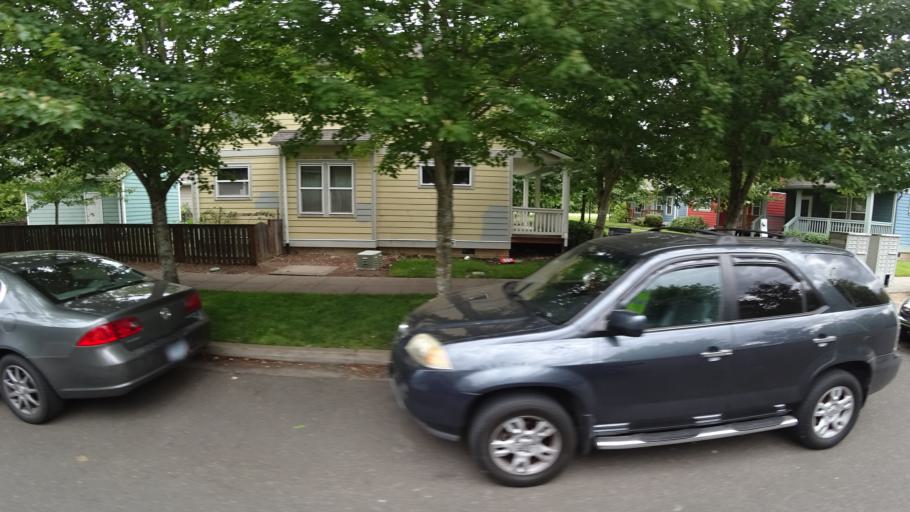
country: US
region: Washington
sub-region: Clark County
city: Vancouver
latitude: 45.5904
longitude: -122.7138
